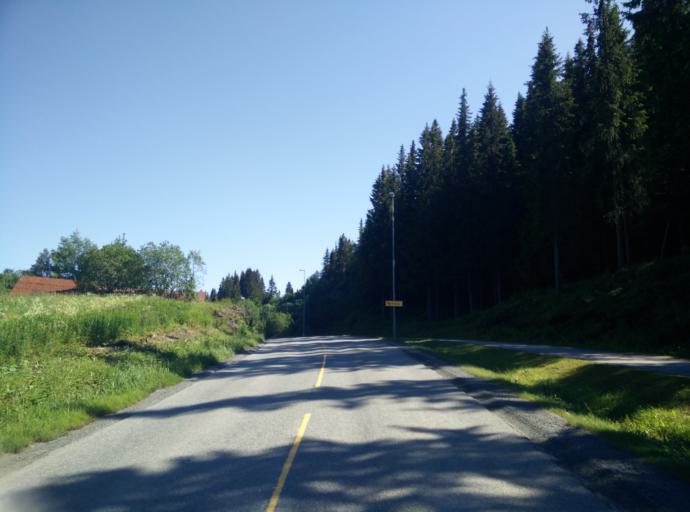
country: NO
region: Sor-Trondelag
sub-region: Trondheim
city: Trondheim
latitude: 63.3768
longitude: 10.3192
